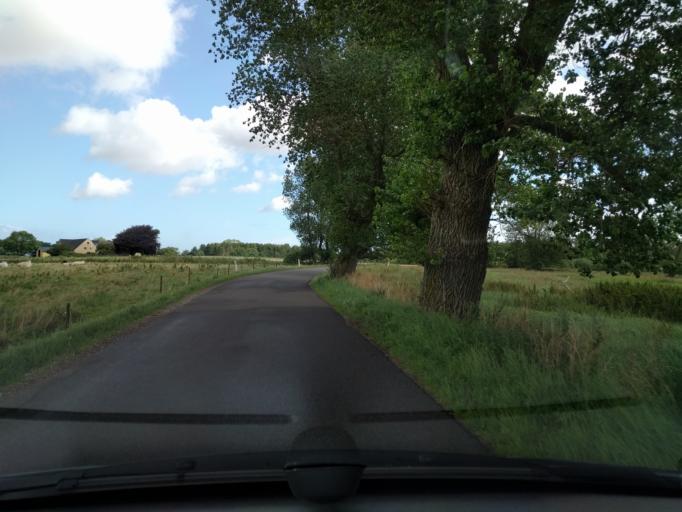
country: DK
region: South Denmark
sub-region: Kerteminde Kommune
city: Langeskov
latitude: 55.3846
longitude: 10.5800
